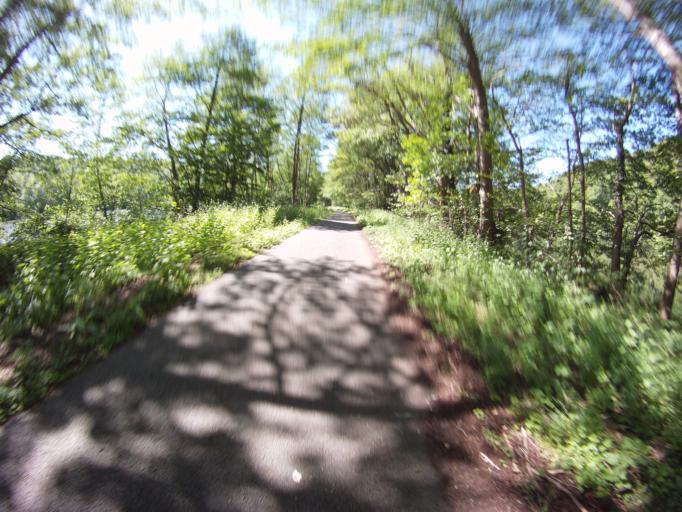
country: FR
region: Lorraine
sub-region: Departement de Meurthe-et-Moselle
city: Velaine-en-Haye
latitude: 48.6576
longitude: 6.0032
